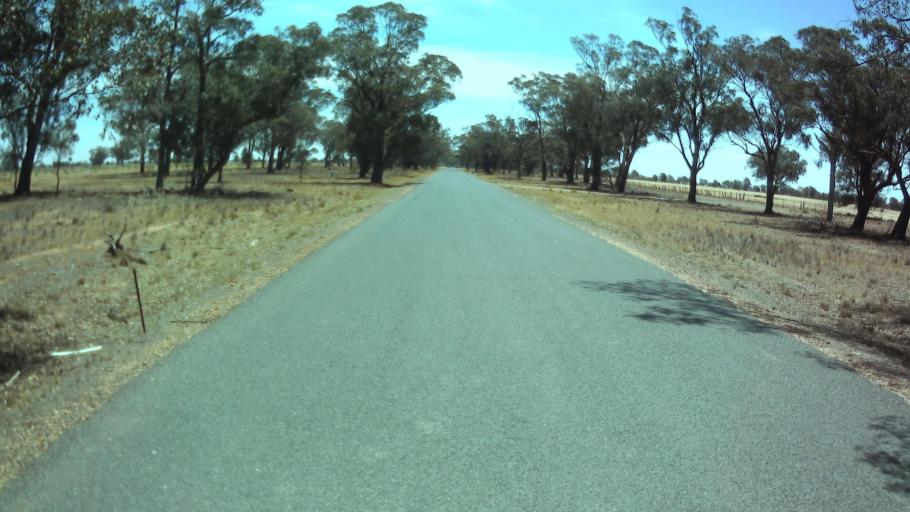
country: AU
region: New South Wales
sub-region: Weddin
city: Grenfell
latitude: -34.0002
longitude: 147.7442
